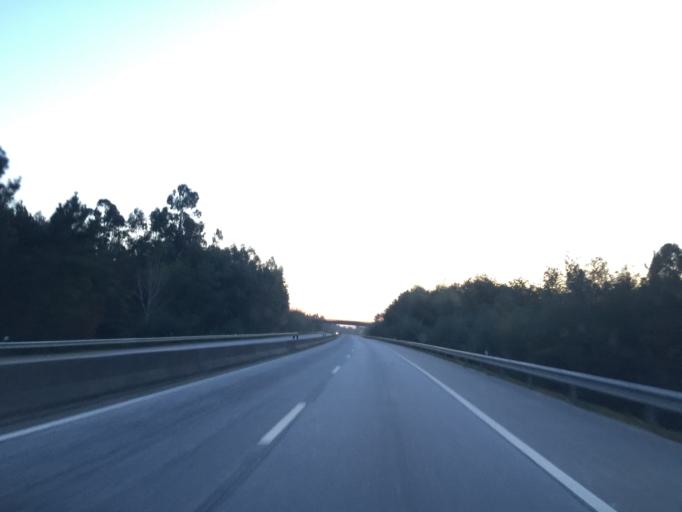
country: PT
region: Coimbra
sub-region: Tabua
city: Tabua
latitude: 40.4093
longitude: -8.0677
